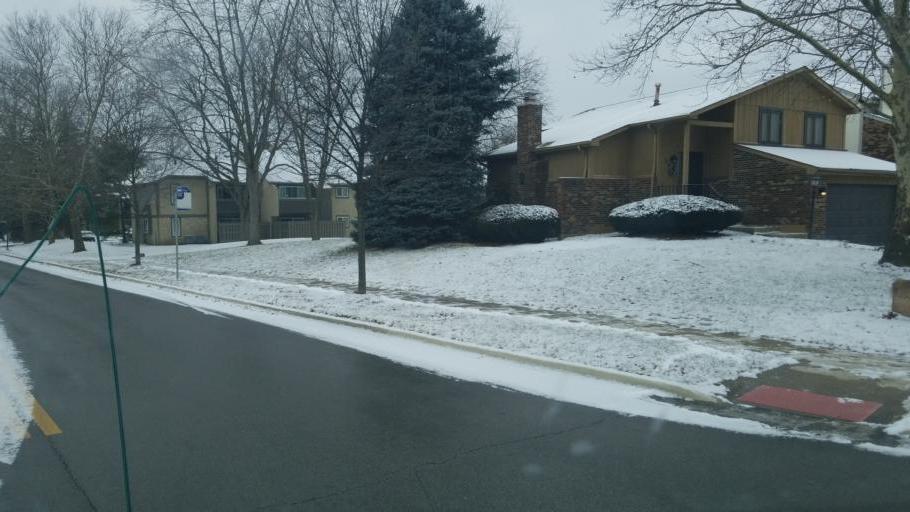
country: US
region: Ohio
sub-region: Delaware County
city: Powell
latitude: 40.1213
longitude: -83.0829
